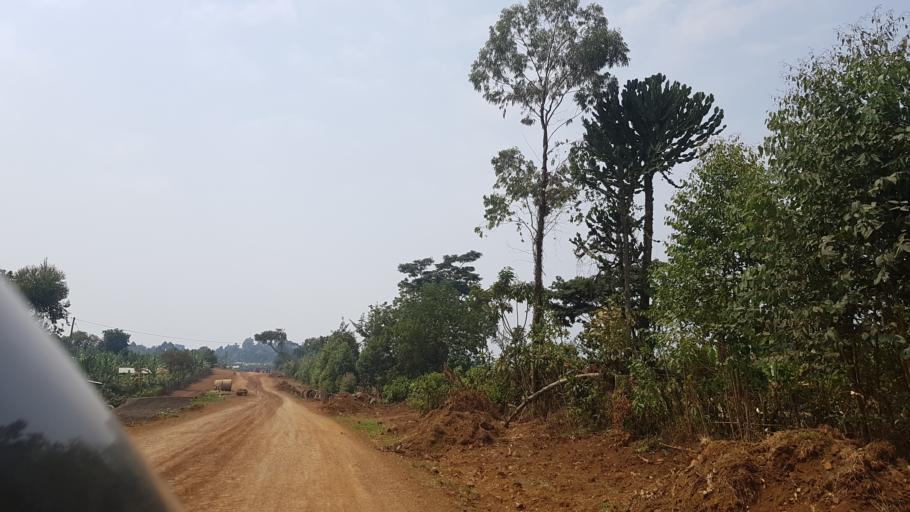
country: ET
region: Oromiya
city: Gore
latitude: 7.8110
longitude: 35.4584
